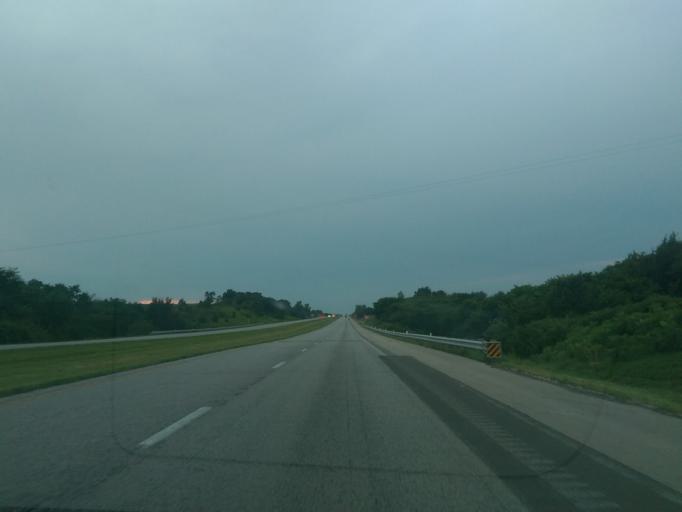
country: US
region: Missouri
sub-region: Holt County
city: Oregon
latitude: 40.0339
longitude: -95.1177
